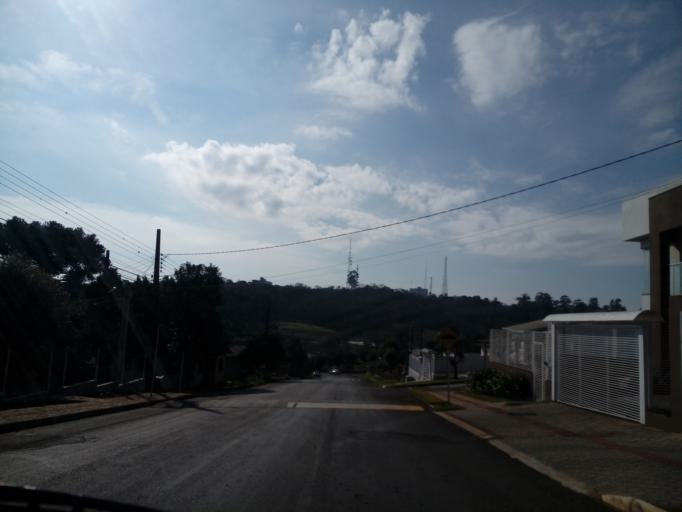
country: BR
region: Santa Catarina
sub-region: Chapeco
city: Chapeco
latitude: -27.1081
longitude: -52.5921
